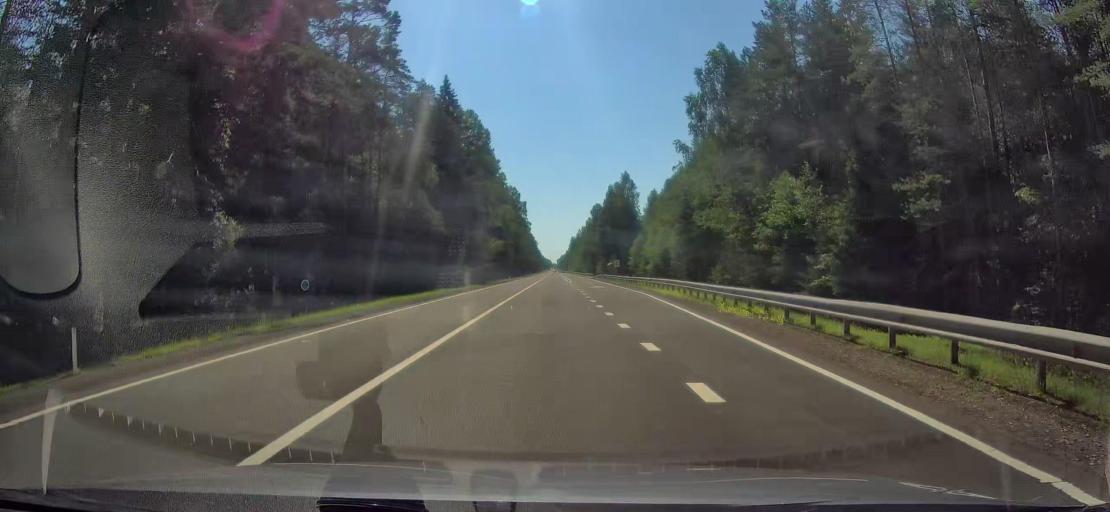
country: RU
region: Leningrad
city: Yefimovskiy
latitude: 59.3798
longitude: 34.7885
